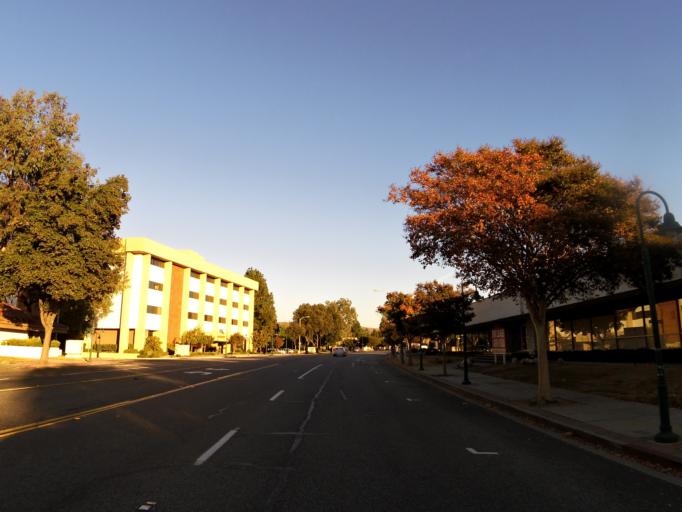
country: US
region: California
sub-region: Ventura County
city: Thousand Oaks
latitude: 34.1792
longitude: -118.8736
